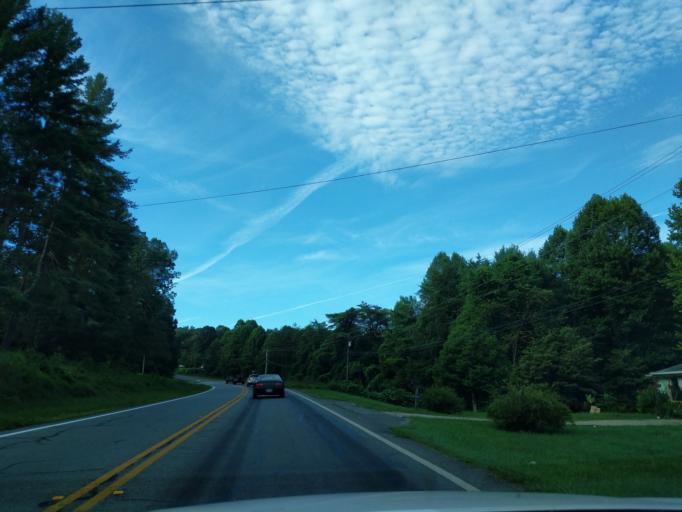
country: US
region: Georgia
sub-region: Fannin County
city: Blue Ridge
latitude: 34.9110
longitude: -84.3769
